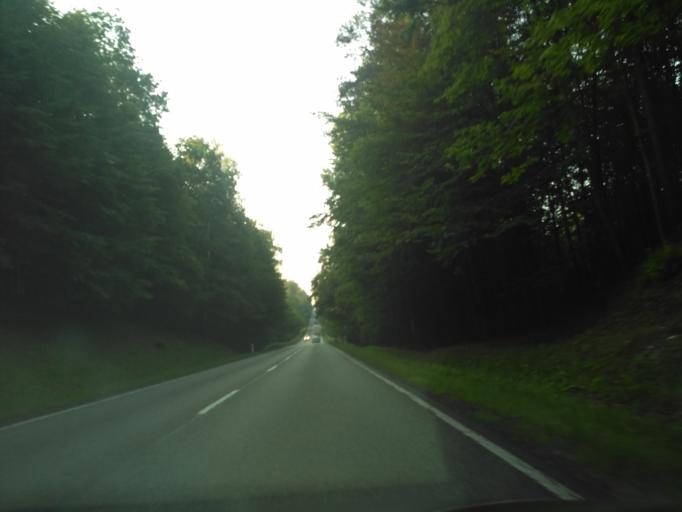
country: PL
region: Lublin Voivodeship
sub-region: Powiat krasnicki
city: Szastarka
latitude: 50.8562
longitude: 22.2840
